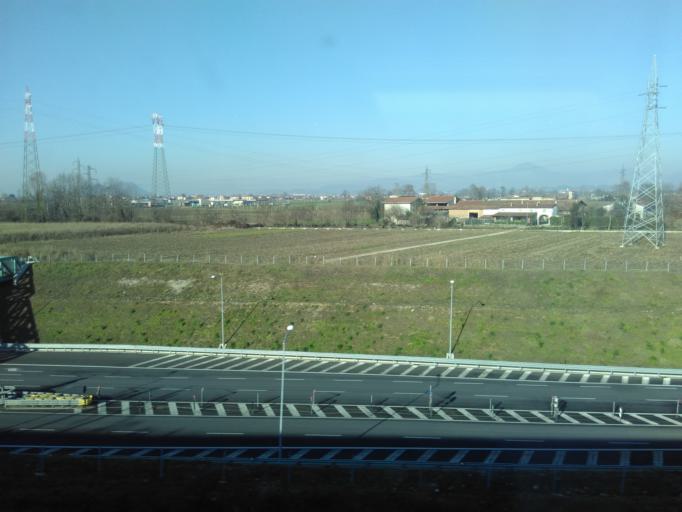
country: IT
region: Lombardy
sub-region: Provincia di Brescia
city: Travagliato
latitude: 45.5328
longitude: 10.0594
